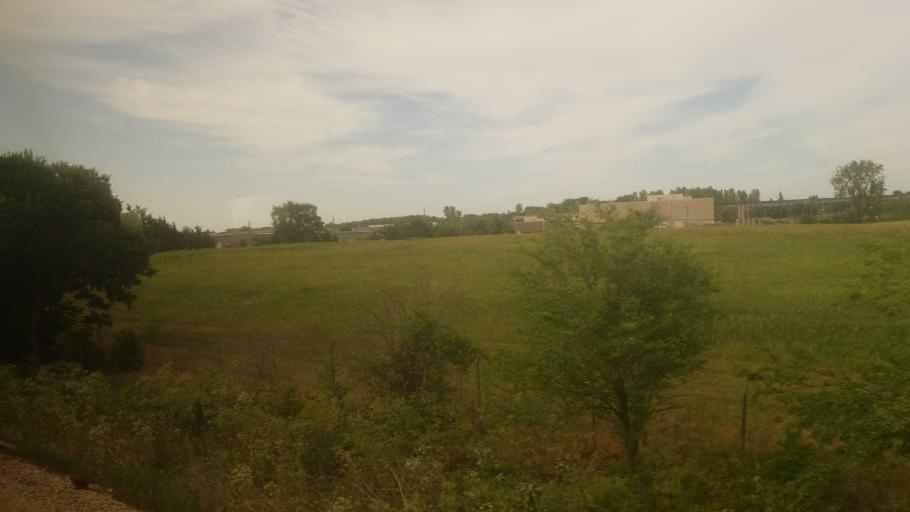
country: US
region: Kansas
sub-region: Douglas County
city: Lawrence
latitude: 38.9518
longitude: -95.1875
